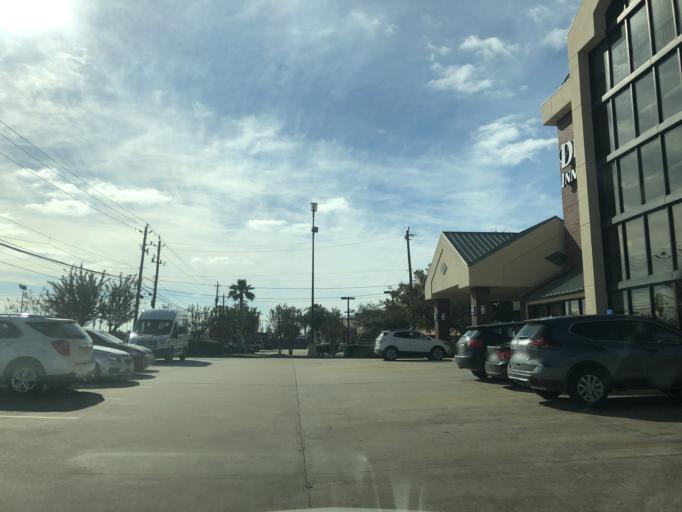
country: US
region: Texas
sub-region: Harris County
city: South Houston
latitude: 29.6549
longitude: -95.2541
